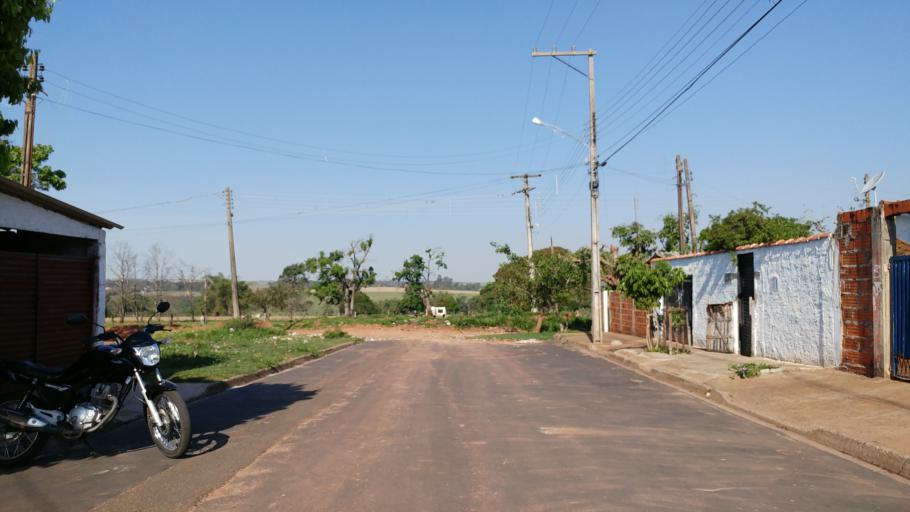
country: BR
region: Sao Paulo
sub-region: Paraguacu Paulista
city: Paraguacu Paulista
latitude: -22.4187
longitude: -50.5667
